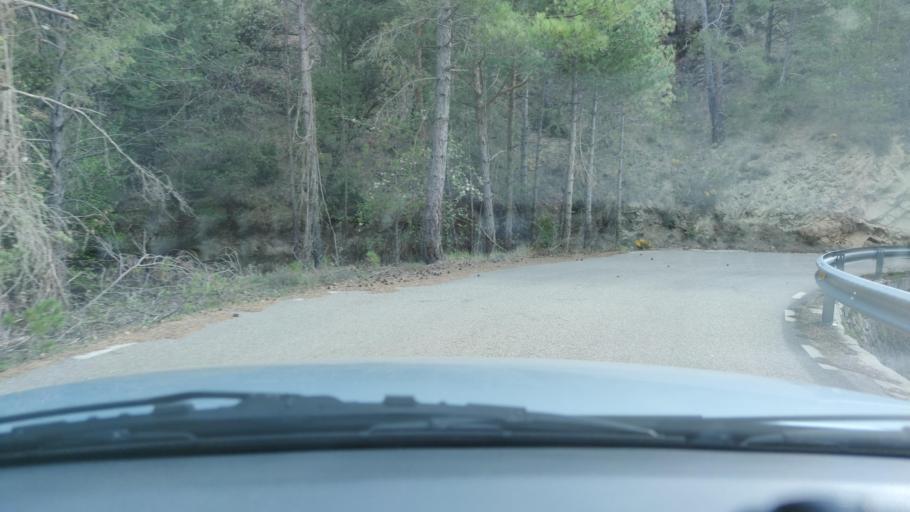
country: ES
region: Catalonia
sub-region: Provincia de Lleida
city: la Seu d'Urgell
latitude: 42.2445
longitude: 1.4301
